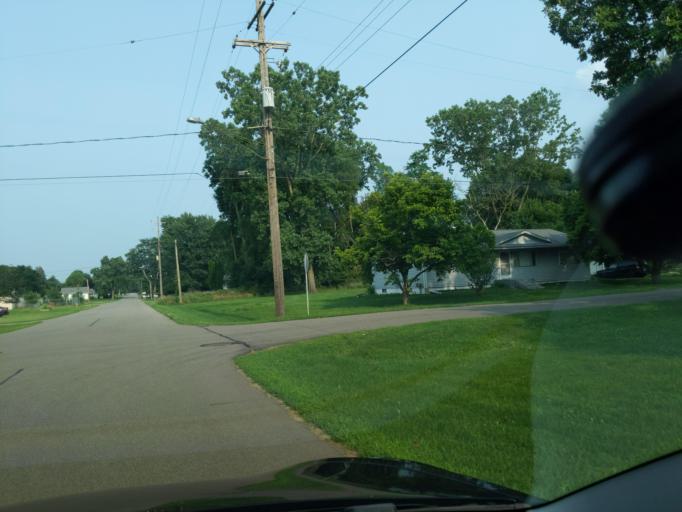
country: US
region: Michigan
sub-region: Jackson County
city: Jackson
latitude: 42.2422
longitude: -84.4395
